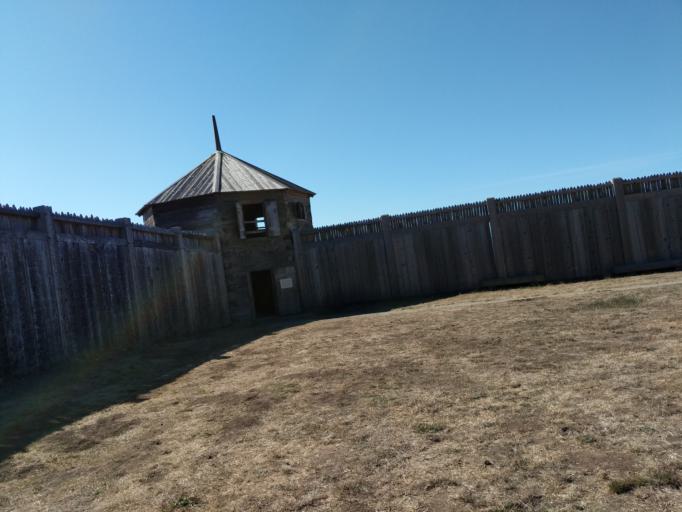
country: US
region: California
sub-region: Sonoma County
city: Monte Rio
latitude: 38.5139
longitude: -123.2433
